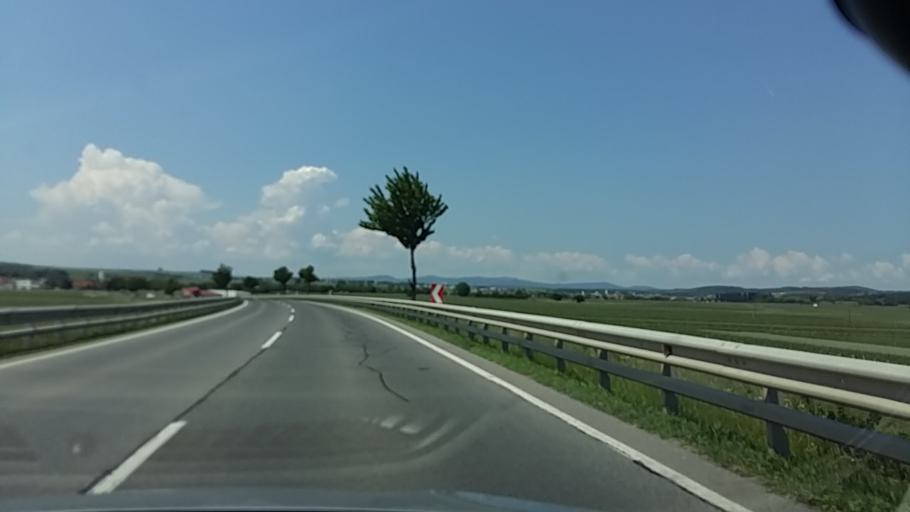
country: AT
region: Burgenland
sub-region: Politischer Bezirk Oberpullendorf
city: Deutschkreutz
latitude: 47.5961
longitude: 16.5945
